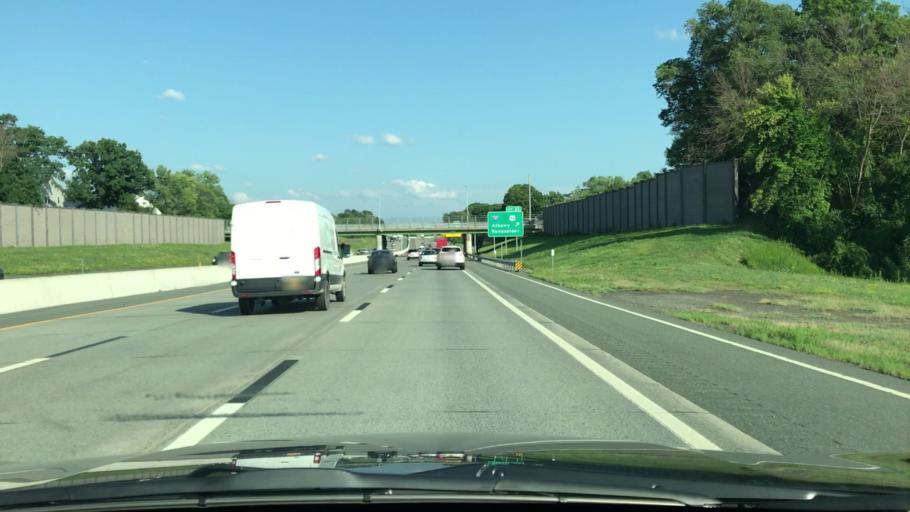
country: US
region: New York
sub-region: Albany County
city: Albany
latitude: 42.6384
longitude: -73.7927
